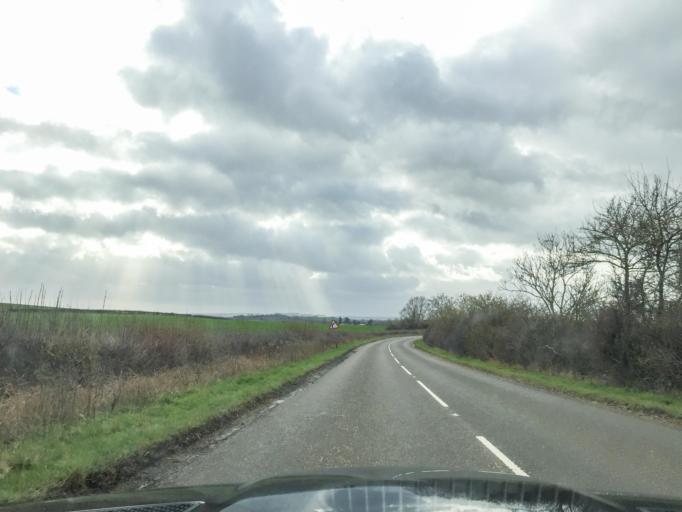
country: GB
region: England
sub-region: Warwickshire
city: Shipston on Stour
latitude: 52.0604
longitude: -1.6015
